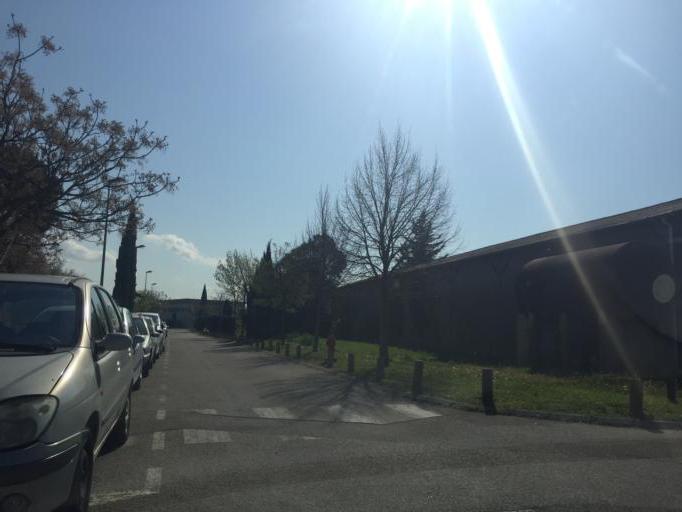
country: FR
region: Provence-Alpes-Cote d'Azur
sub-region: Departement du Vaucluse
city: Montfavet
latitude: 43.9140
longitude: 4.8905
